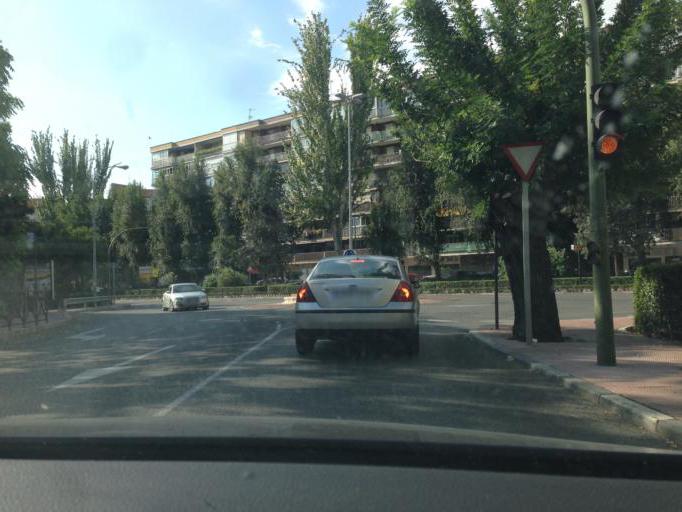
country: ES
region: Madrid
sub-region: Provincia de Madrid
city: Alcala de Henares
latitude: 40.4917
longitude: -3.3777
